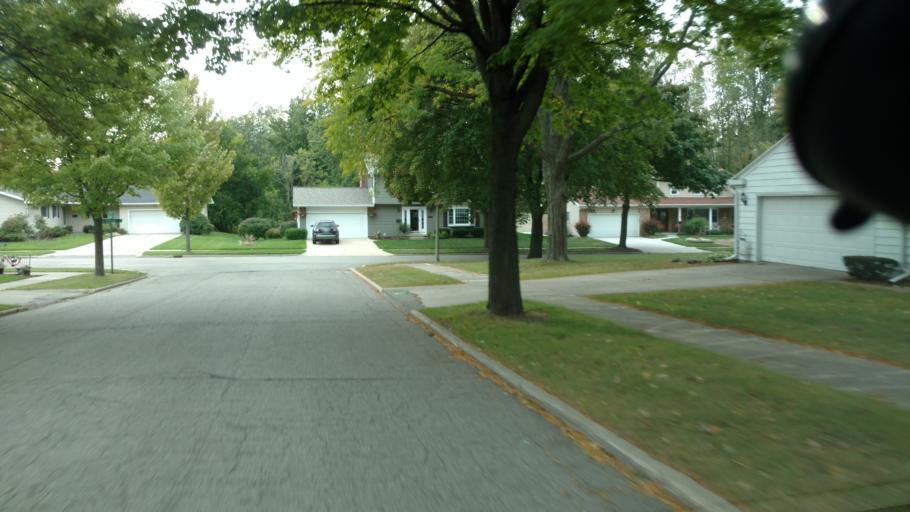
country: US
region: Michigan
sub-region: Ingham County
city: East Lansing
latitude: 42.7513
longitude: -84.5106
